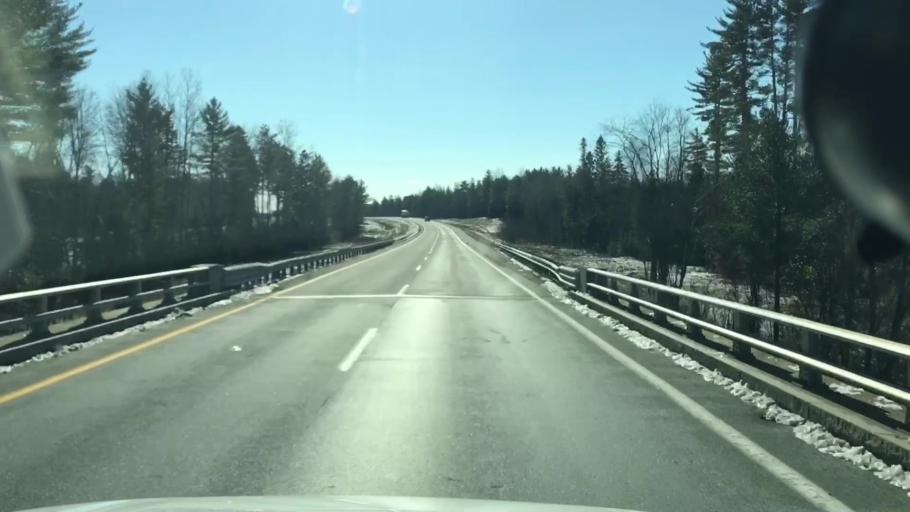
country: US
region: Maine
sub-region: Penobscot County
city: Howland
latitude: 45.2649
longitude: -68.6805
